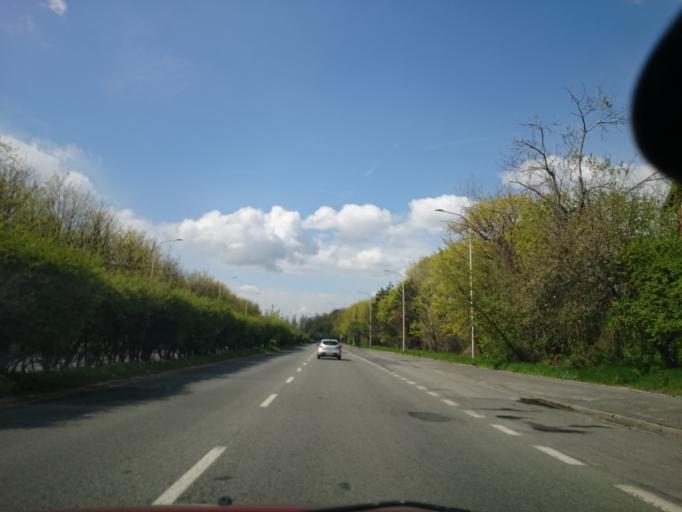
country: PL
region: Opole Voivodeship
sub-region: Powiat opolski
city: Opole
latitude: 50.6728
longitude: 17.9375
